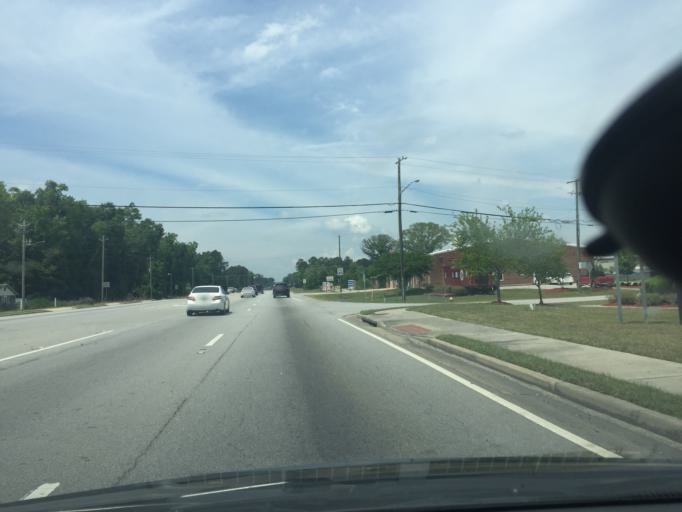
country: US
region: Georgia
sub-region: Chatham County
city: Bloomingdale
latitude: 32.1333
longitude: -81.3017
